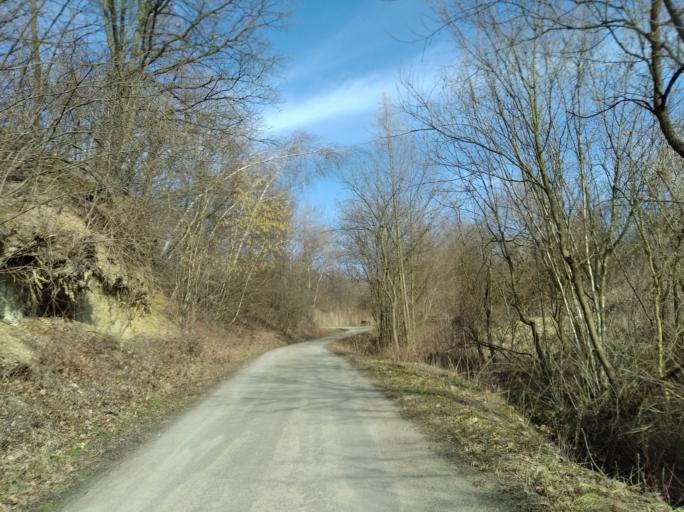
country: PL
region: Subcarpathian Voivodeship
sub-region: Powiat brzozowski
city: Gorki
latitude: 49.6428
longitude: 22.0524
